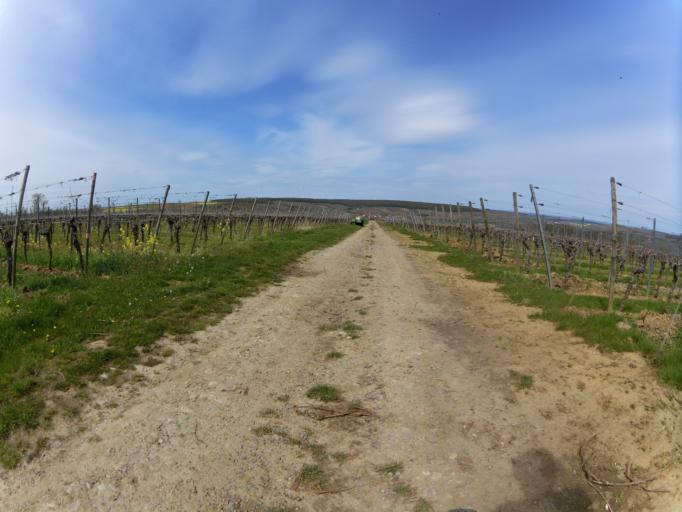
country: DE
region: Bavaria
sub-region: Regierungsbezirk Unterfranken
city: Nordheim
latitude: 49.8645
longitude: 10.1605
